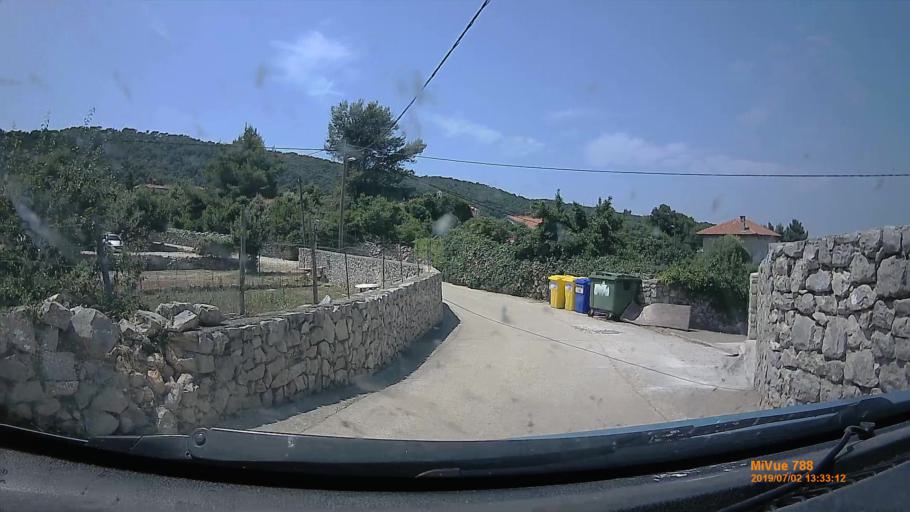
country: HR
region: Primorsko-Goranska
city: Mali Losinj
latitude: 44.5148
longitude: 14.5075
